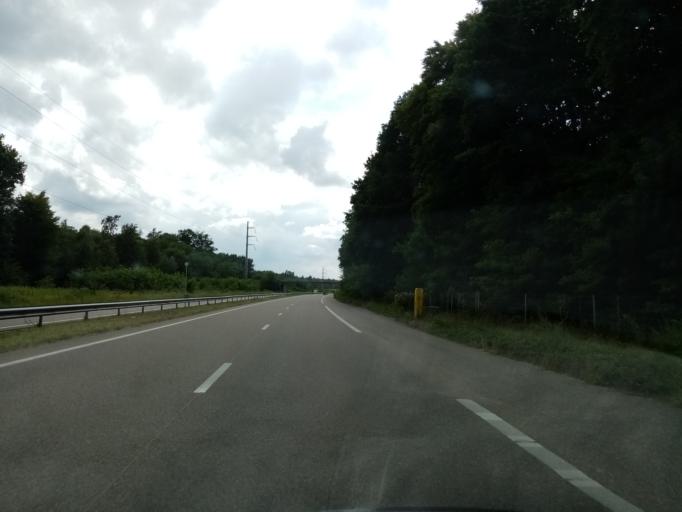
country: FR
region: Alsace
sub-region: Departement du Bas-Rhin
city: Seltz
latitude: 48.9085
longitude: 8.1059
